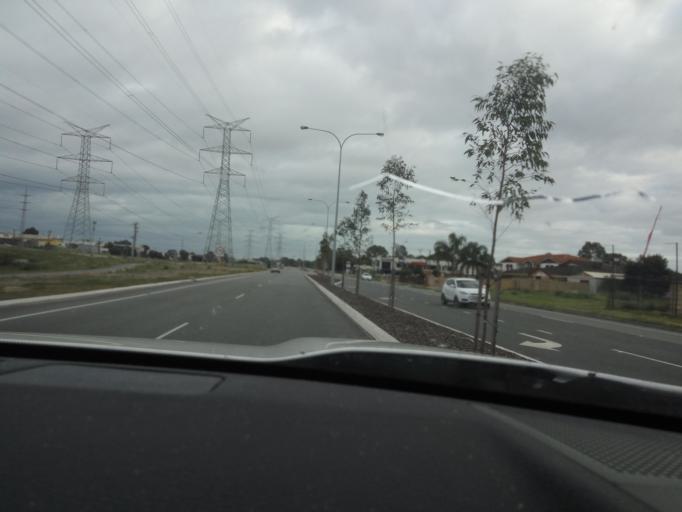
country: AU
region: Western Australia
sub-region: City of Cockburn
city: South Lake
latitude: -32.1212
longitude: 115.8482
